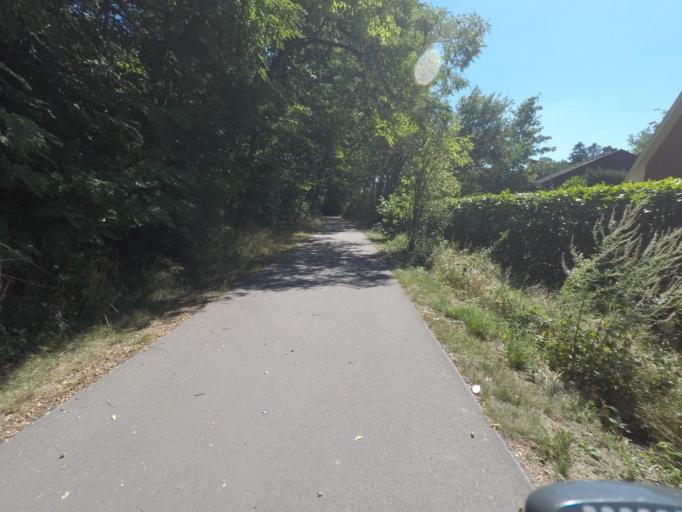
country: DE
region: Schleswig-Holstein
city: Lutjensee
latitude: 53.6417
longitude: 10.3688
